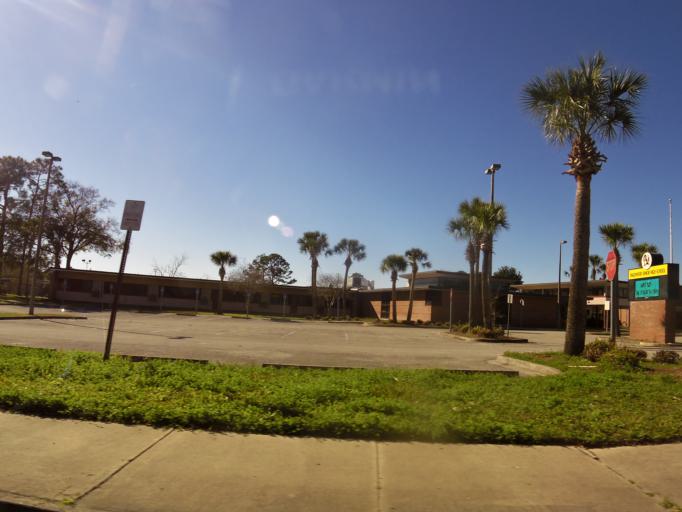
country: US
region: Florida
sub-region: Duval County
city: Jacksonville
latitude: 30.2776
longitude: -81.6100
